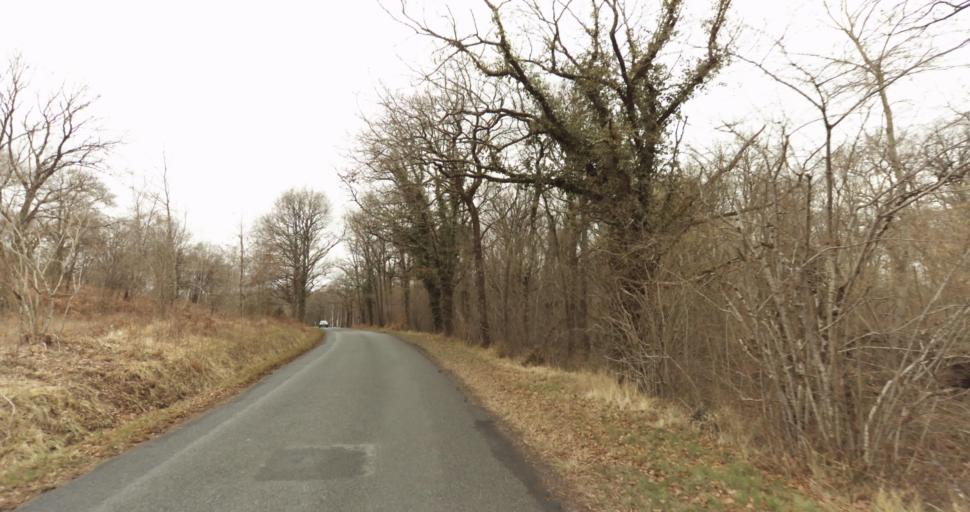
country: FR
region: Pays de la Loire
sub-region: Departement de Maine-et-Loire
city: Distre
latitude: 47.2557
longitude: -0.1274
